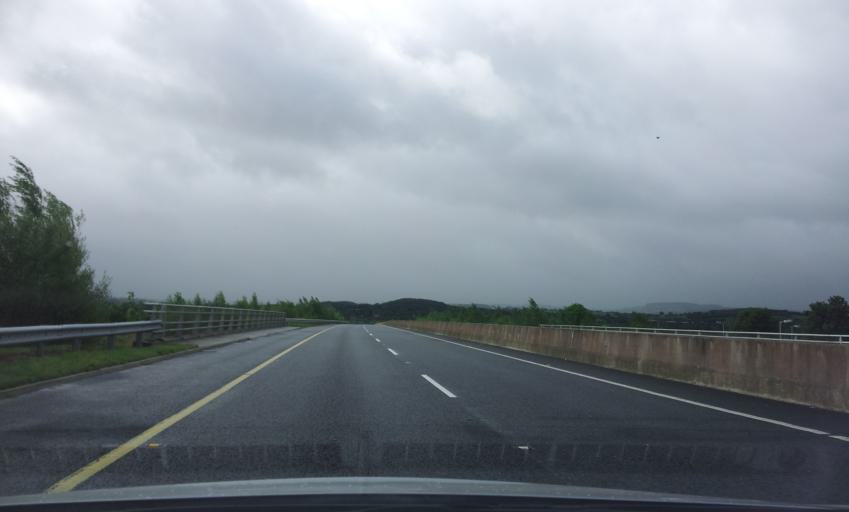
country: IE
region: Leinster
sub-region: Kilkenny
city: Thomastown
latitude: 52.4864
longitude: -7.2406
